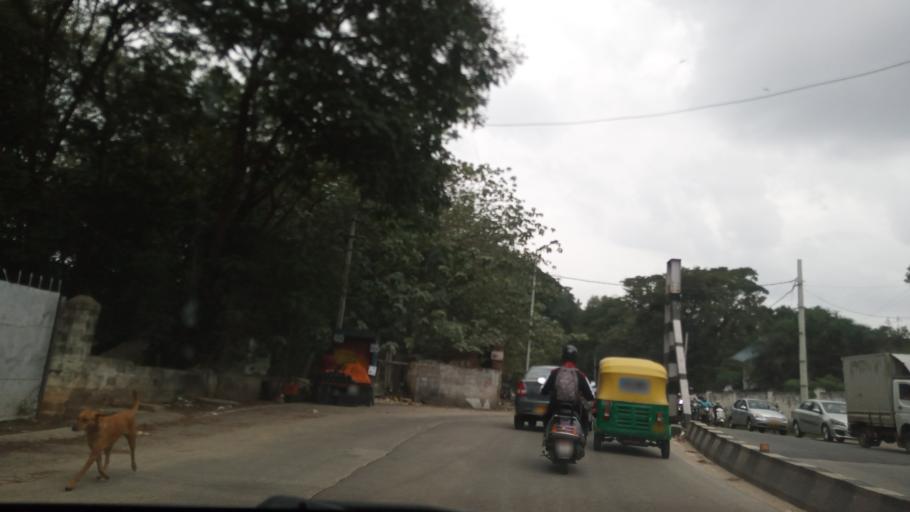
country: IN
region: Karnataka
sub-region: Bangalore Urban
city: Bangalore
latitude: 12.9958
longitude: 77.5959
